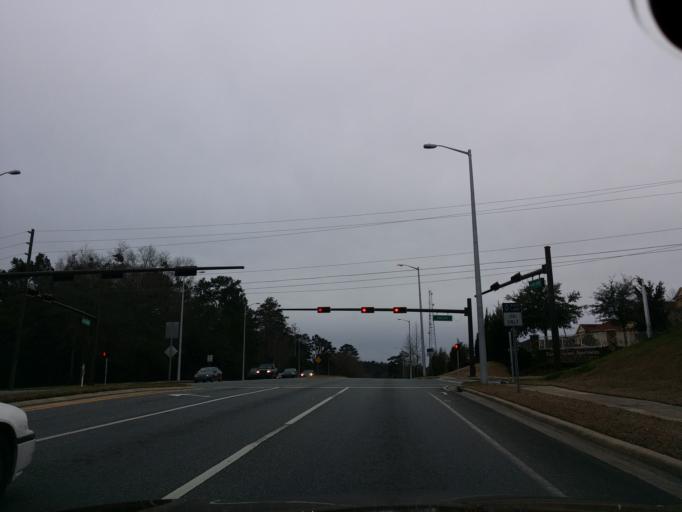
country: US
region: Florida
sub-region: Leon County
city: Tallahassee
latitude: 30.4610
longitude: -84.2428
